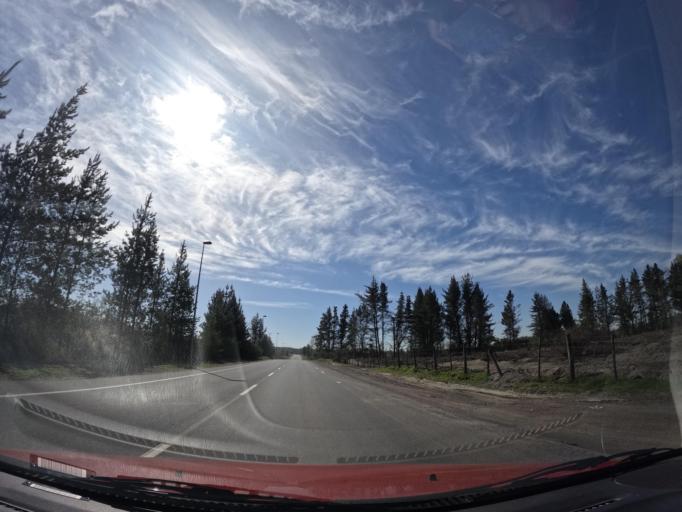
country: CL
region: Biobio
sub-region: Provincia de Biobio
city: Cabrero
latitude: -36.9390
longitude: -72.3455
